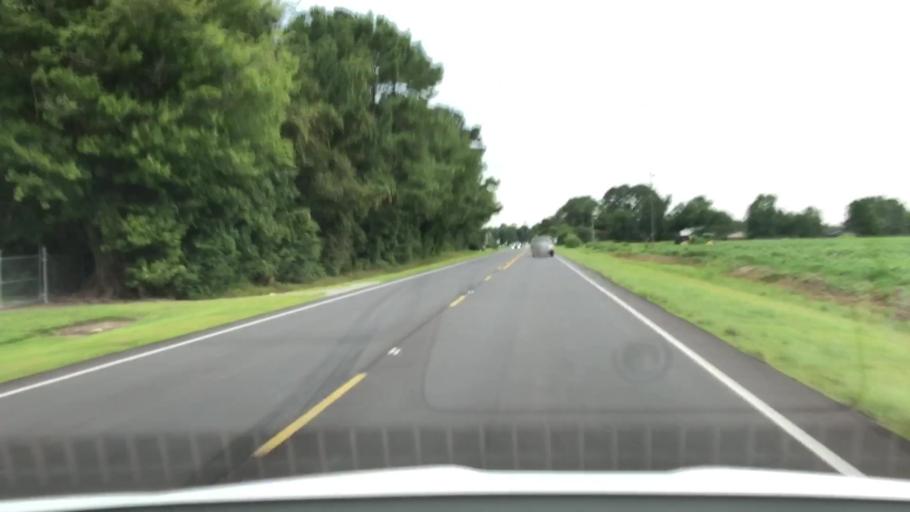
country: US
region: North Carolina
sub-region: Jones County
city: Maysville
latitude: 34.8961
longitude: -77.2195
